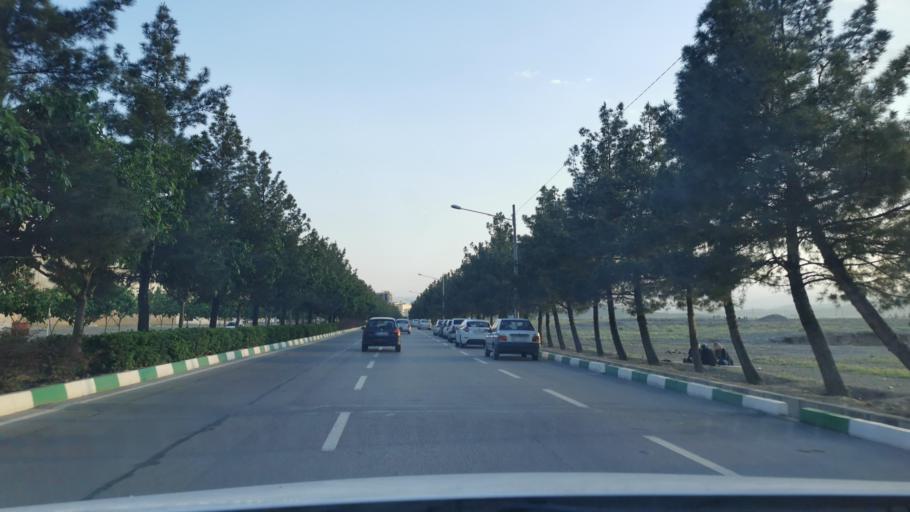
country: IR
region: Razavi Khorasan
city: Torqabeh
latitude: 36.3848
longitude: 59.4643
